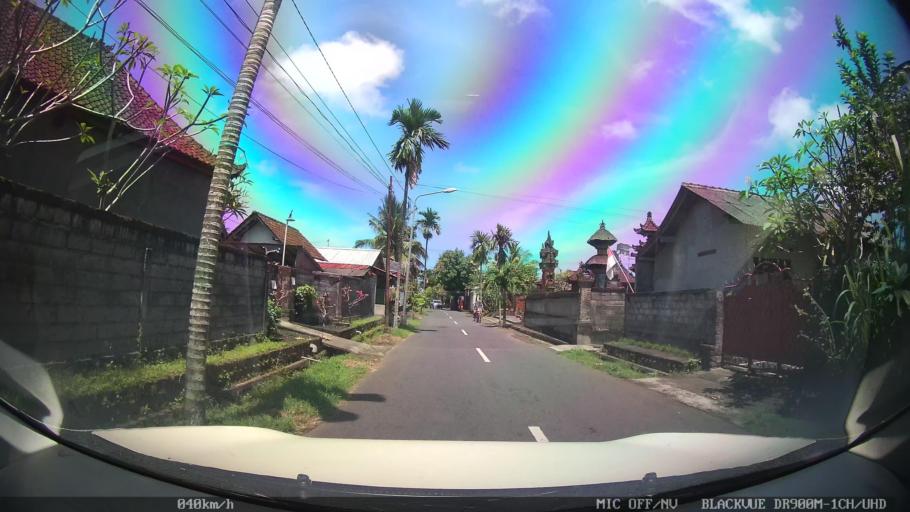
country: ID
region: Bali
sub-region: Kabupaten Gianyar
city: Ubud
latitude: -8.5551
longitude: 115.3158
